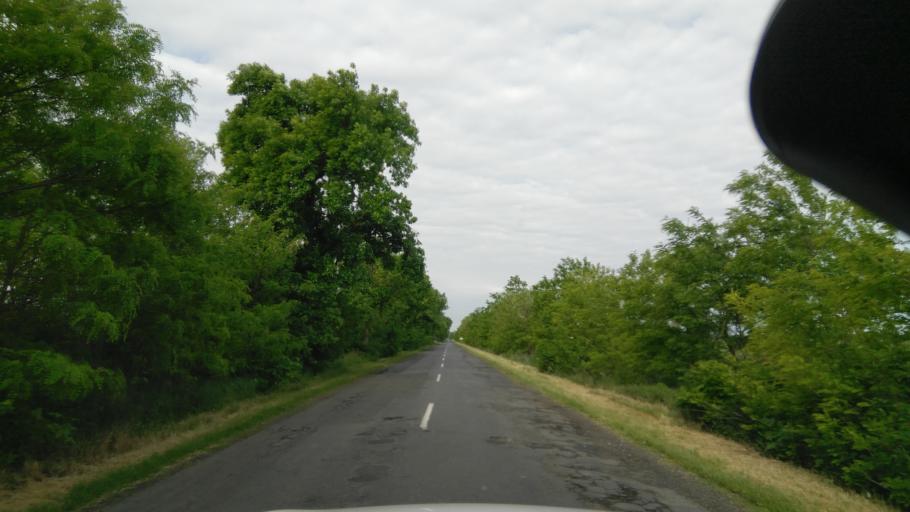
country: HU
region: Bekes
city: Ketegyhaza
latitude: 46.5335
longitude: 21.1194
